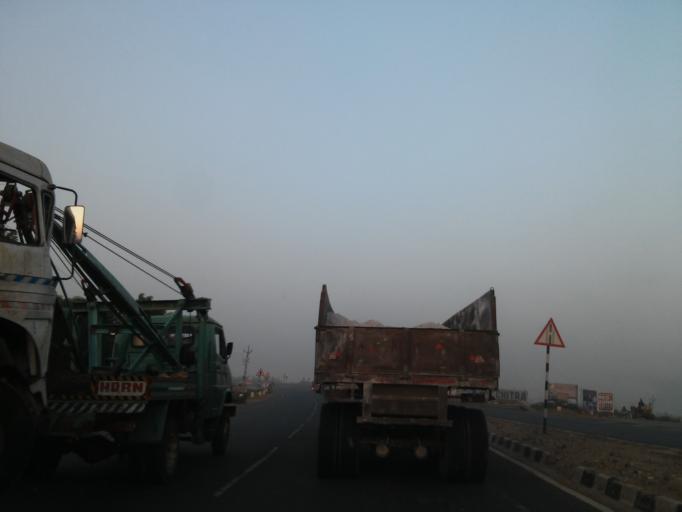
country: IN
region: Gujarat
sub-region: Surendranagar
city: Halvad
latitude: 23.0153
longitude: 71.2043
